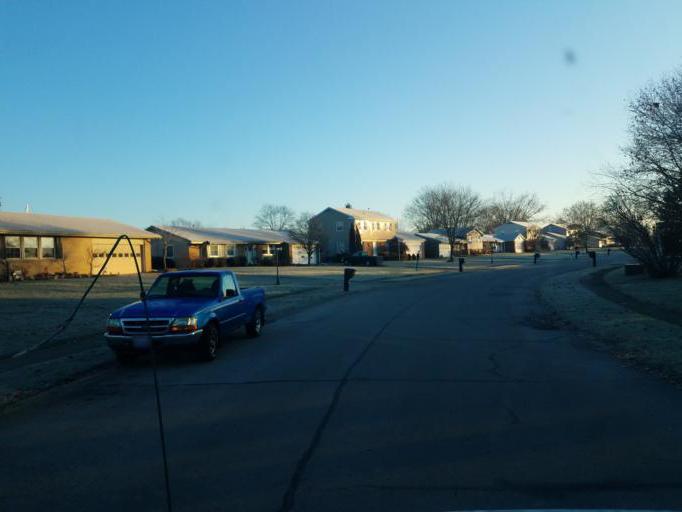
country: US
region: Ohio
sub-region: Marion County
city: Marion
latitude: 40.5688
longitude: -83.1004
